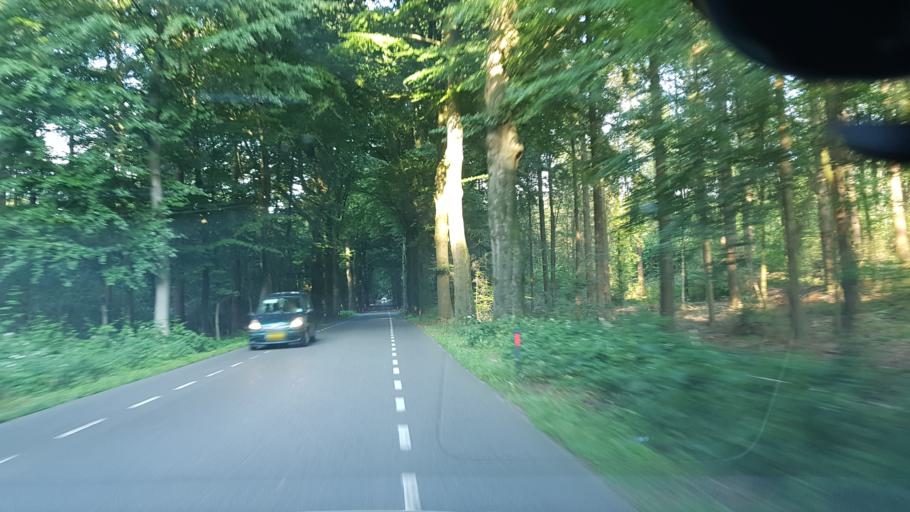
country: NL
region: Gelderland
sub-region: Gemeente Groesbeek
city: Groesbeek
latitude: 51.7743
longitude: 5.9076
